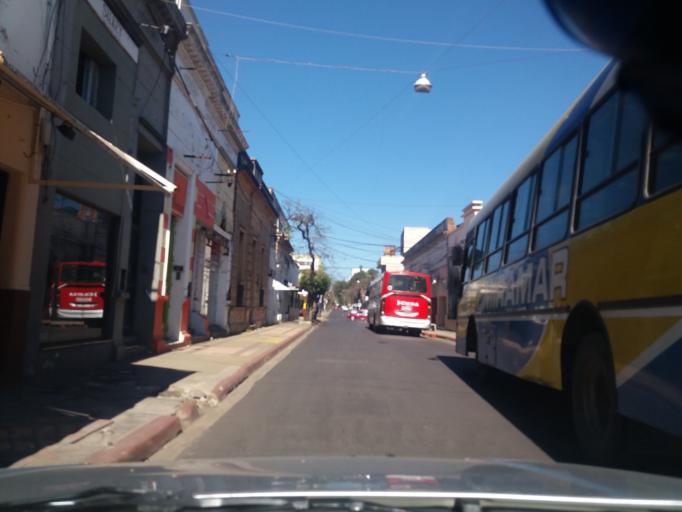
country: AR
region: Corrientes
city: Corrientes
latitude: -27.4678
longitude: -58.8392
